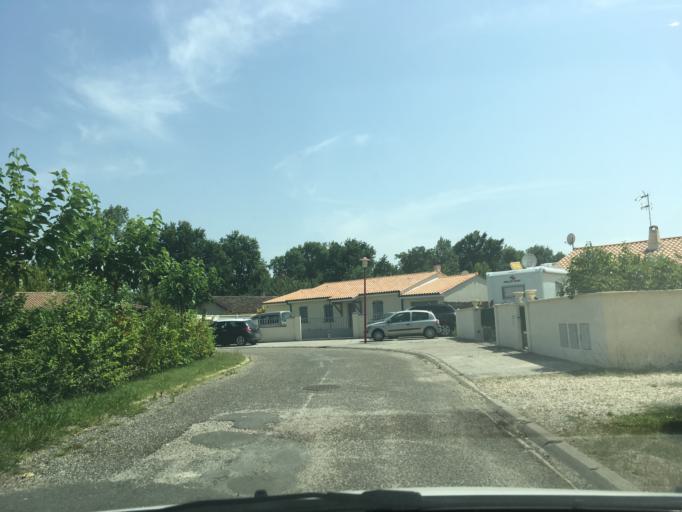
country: FR
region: Aquitaine
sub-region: Departement de la Gironde
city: Cantenac
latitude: 45.0255
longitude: -0.6344
